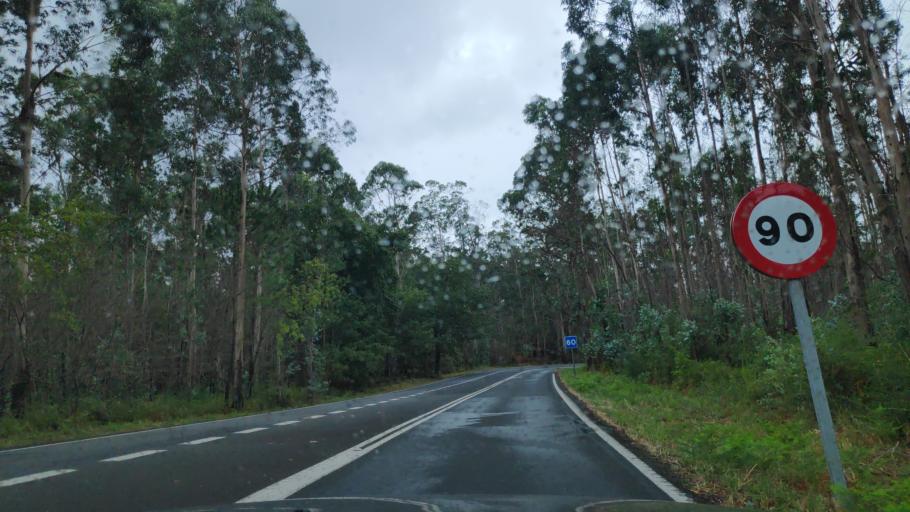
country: ES
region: Galicia
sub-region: Provincia de Pontevedra
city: Catoira
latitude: 42.6954
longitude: -8.7577
